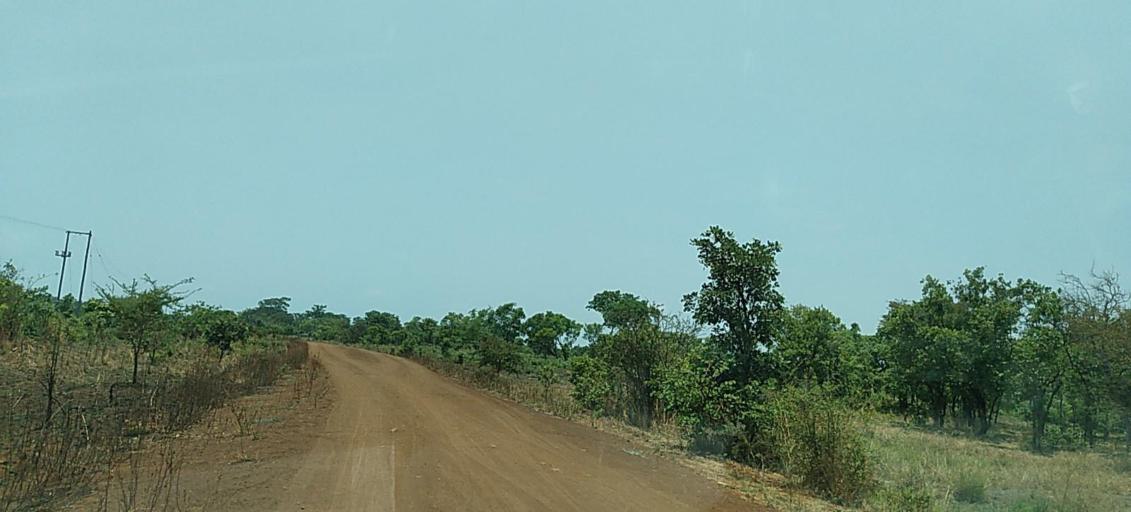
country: ZM
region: Copperbelt
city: Mpongwe
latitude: -13.7010
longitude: 27.8673
